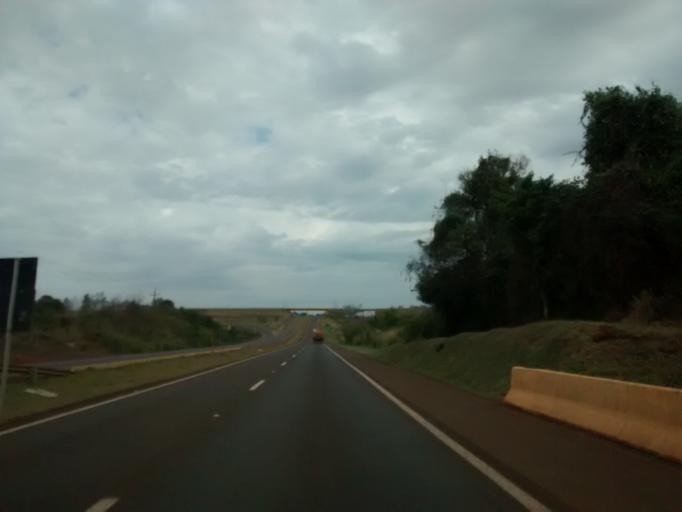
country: BR
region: Parana
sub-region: Campo Mourao
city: Campo Mourao
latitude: -23.9823
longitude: -52.3559
